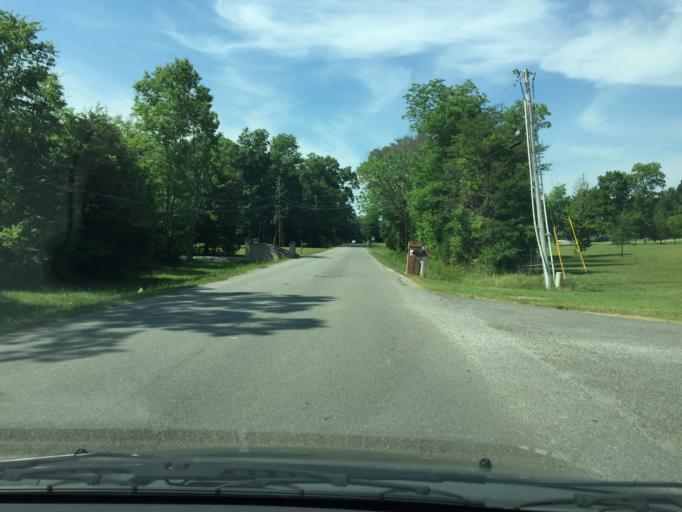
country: US
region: Tennessee
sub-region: Hamilton County
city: Collegedale
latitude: 35.1216
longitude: -84.9968
